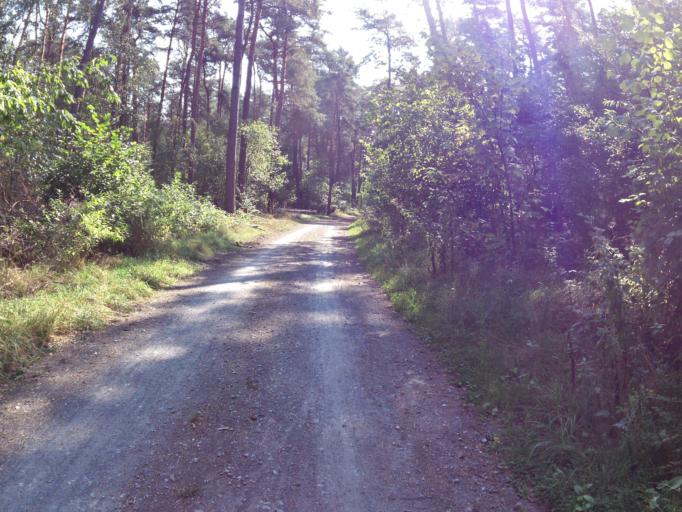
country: DE
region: North Rhine-Westphalia
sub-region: Regierungsbezirk Detmold
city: Harsewinkel
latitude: 51.9370
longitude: 8.2683
